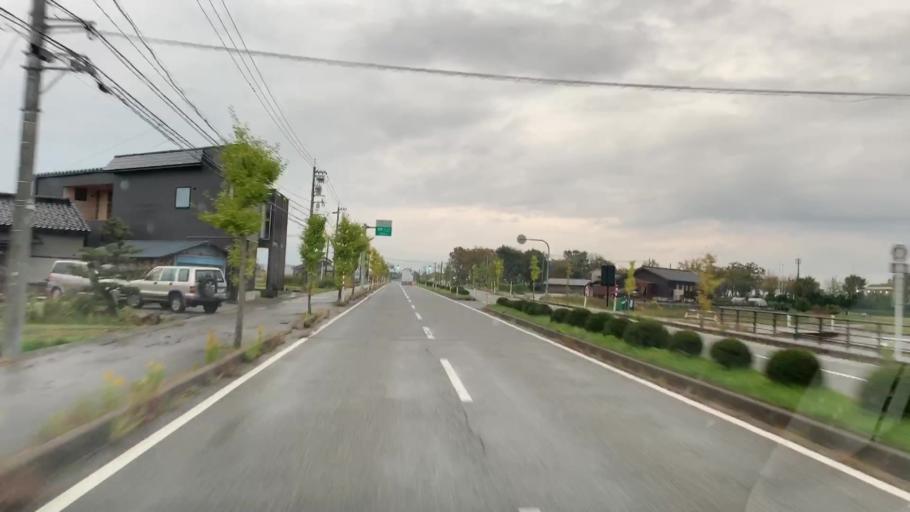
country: JP
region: Toyama
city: Kamiichi
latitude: 36.6840
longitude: 137.3325
